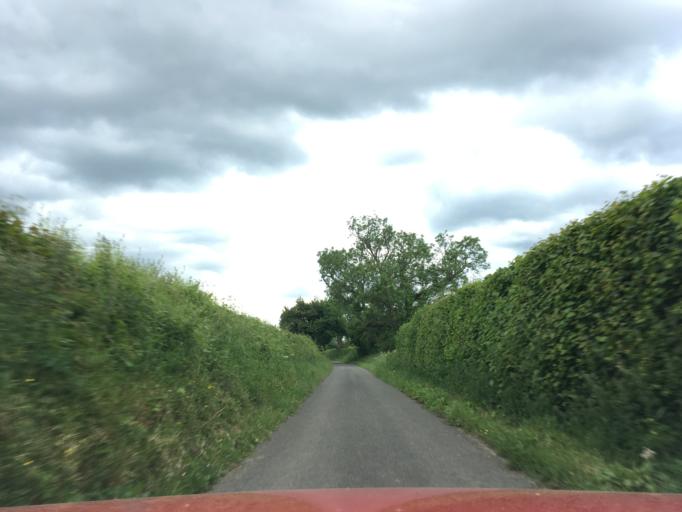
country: GB
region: England
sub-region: Wiltshire
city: Hankerton
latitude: 51.6562
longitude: -2.0215
